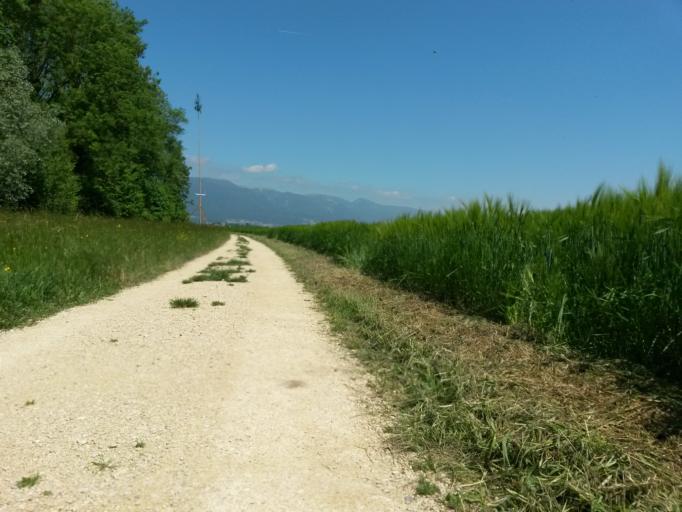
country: CH
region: Bern
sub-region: Biel/Bienne District
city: Meinisberg
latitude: 47.1300
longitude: 7.3477
